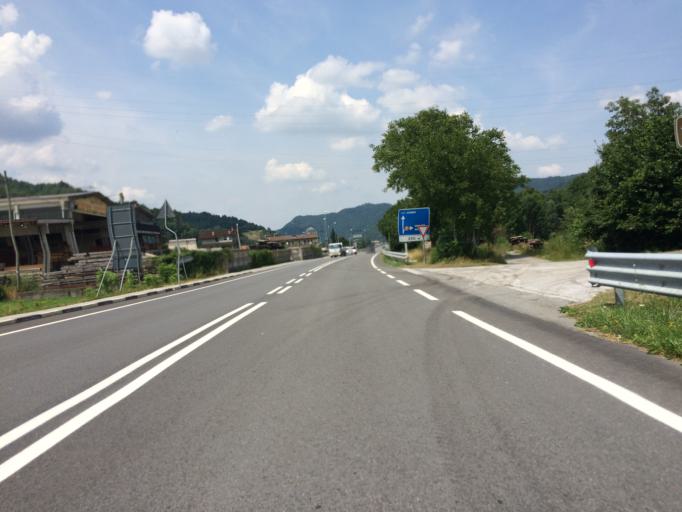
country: IT
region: Piedmont
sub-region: Provincia di Cuneo
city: Robilante
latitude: 44.2773
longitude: 7.5179
